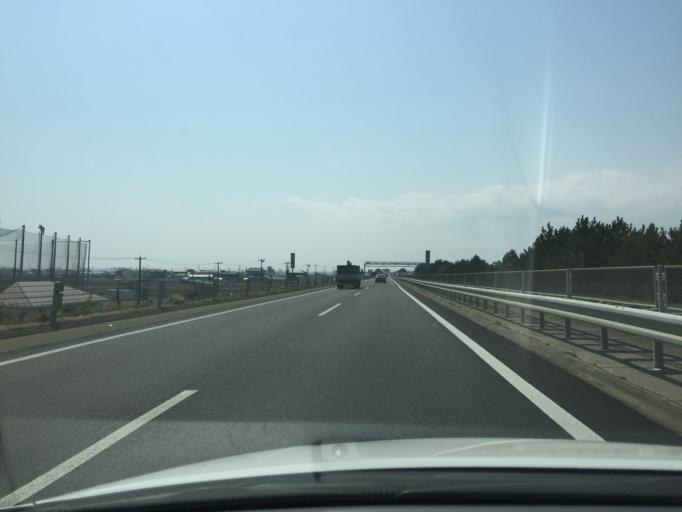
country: JP
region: Miyagi
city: Sendai-shi
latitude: 38.2271
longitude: 140.9528
